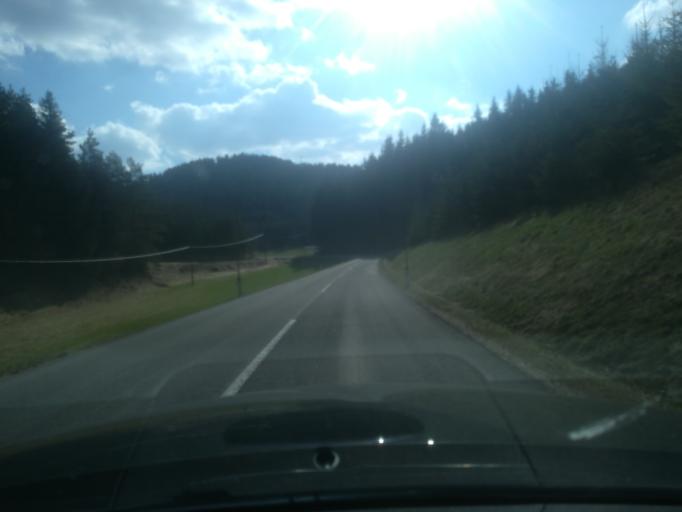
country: AT
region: Lower Austria
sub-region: Politischer Bezirk Zwettl
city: Langschlag
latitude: 48.4637
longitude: 14.7130
